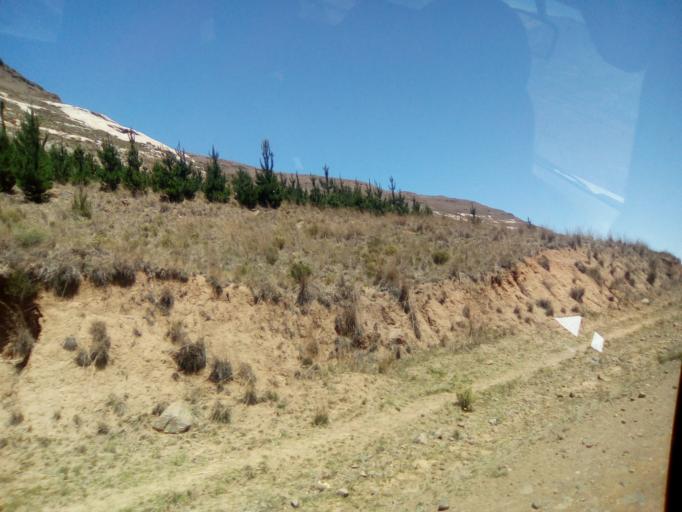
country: LS
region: Qacha's Nek
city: Qacha's Nek
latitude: -30.0373
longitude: 28.6796
